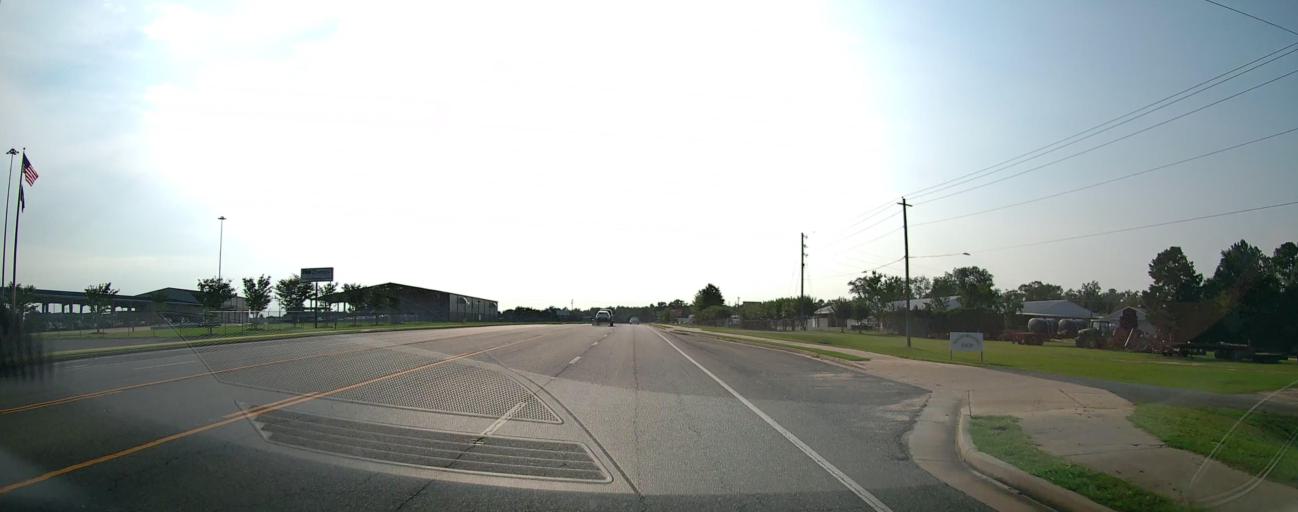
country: US
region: Georgia
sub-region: Taylor County
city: Reynolds
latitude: 32.5603
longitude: -84.1057
